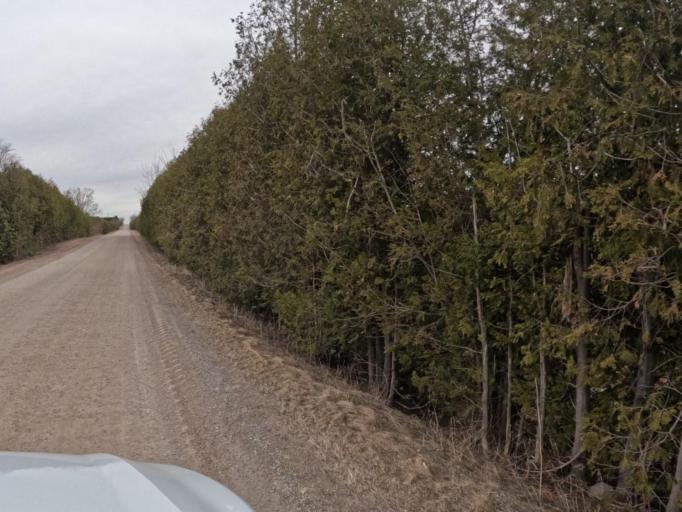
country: CA
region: Ontario
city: Orangeville
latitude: 43.9242
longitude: -80.2563
